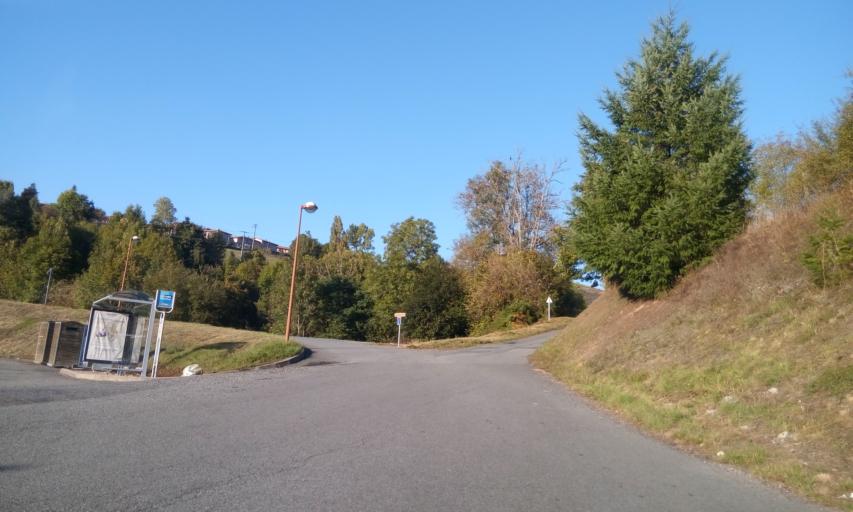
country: FR
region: Rhone-Alpes
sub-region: Departement du Rhone
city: Tarare
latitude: 45.9411
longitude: 4.4351
